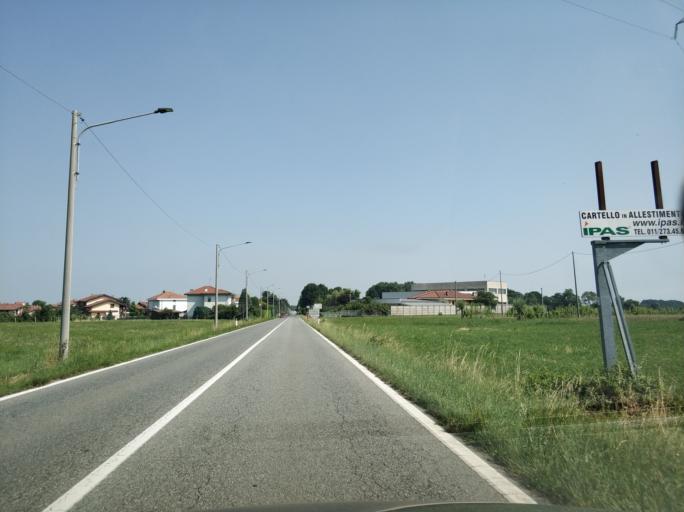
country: IT
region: Piedmont
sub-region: Provincia di Torino
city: Oglianico
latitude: 45.3470
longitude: 7.7054
